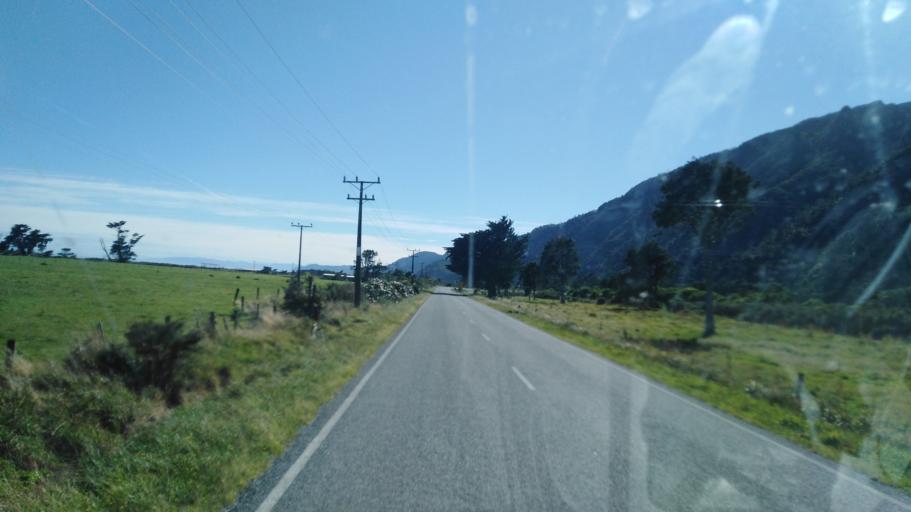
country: NZ
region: West Coast
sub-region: Buller District
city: Westport
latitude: -41.6551
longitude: 171.8255
